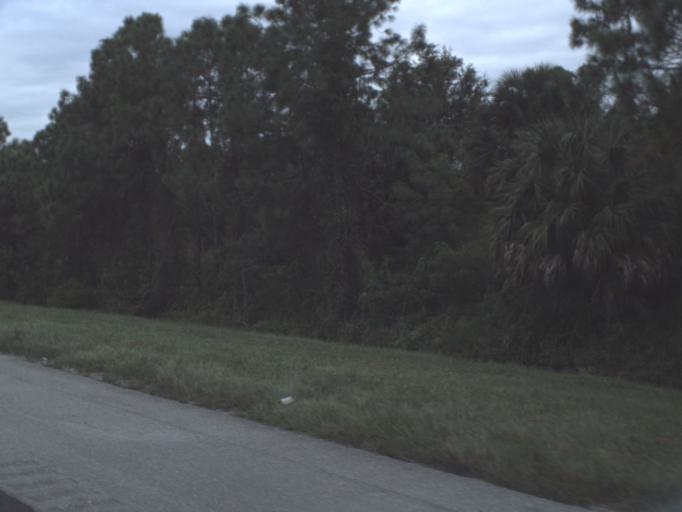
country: US
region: Florida
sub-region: Collier County
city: Vineyards
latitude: 26.2007
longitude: -81.7361
